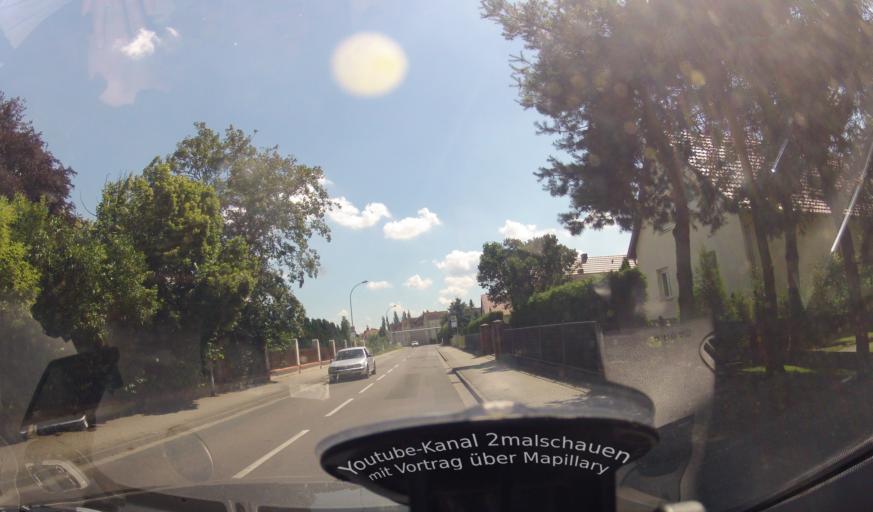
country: DE
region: Saxony
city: Torgau
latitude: 51.5711
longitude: 12.9949
